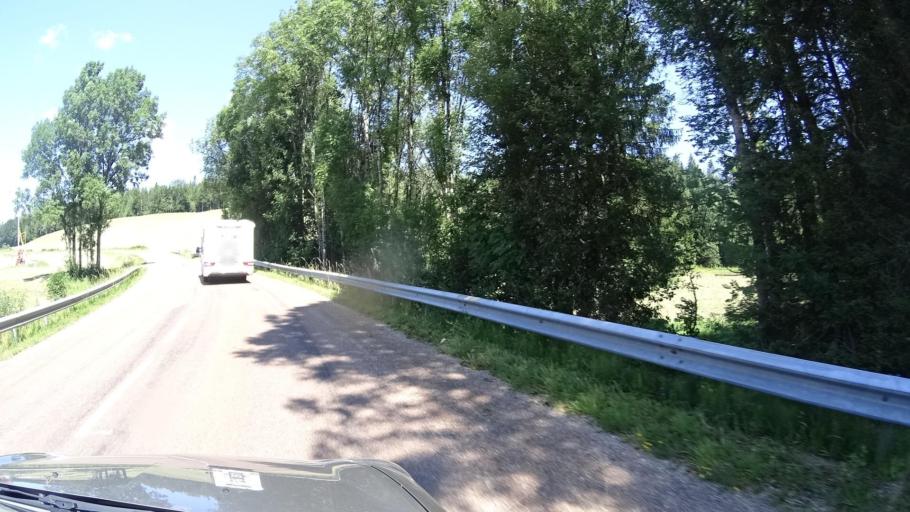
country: FR
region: Franche-Comte
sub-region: Departement du Jura
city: Longchaumois
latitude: 46.5080
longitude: 5.9017
